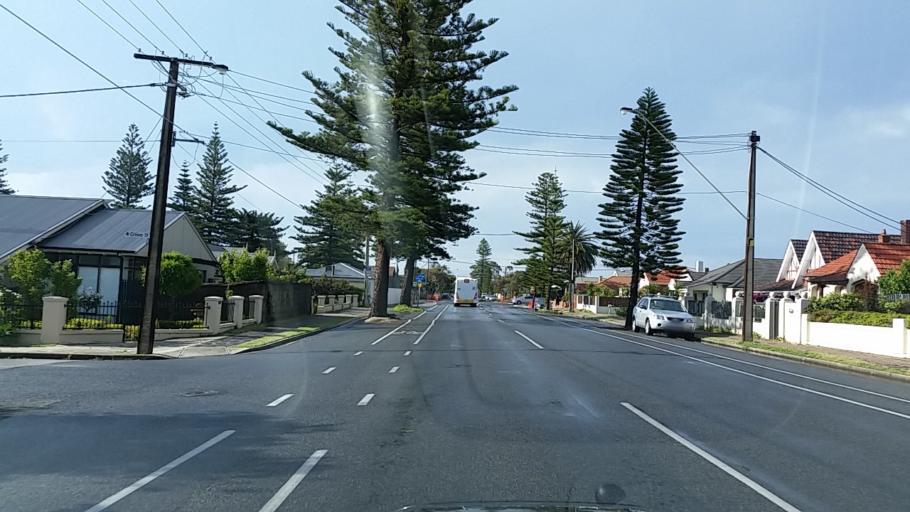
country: AU
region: South Australia
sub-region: Charles Sturt
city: Henley Beach
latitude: -34.9148
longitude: 138.4969
